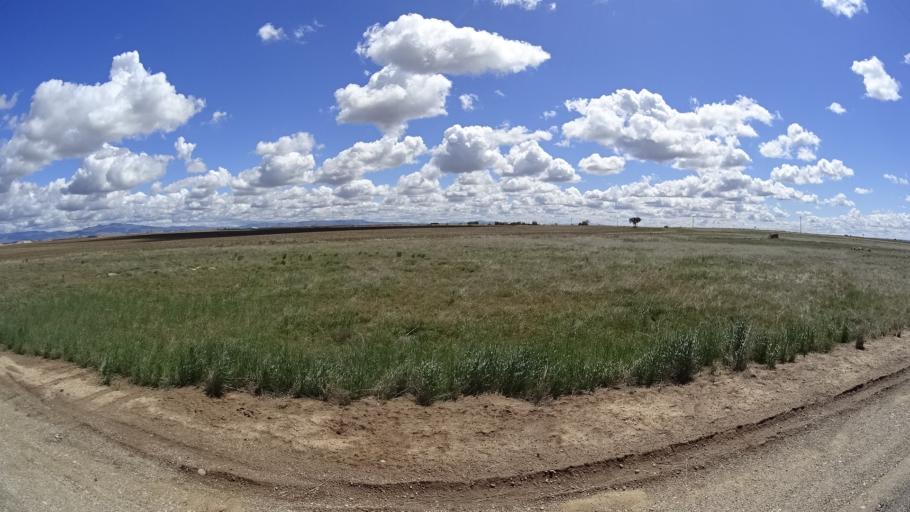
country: US
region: Idaho
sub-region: Ada County
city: Kuna
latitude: 43.4607
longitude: -116.2744
